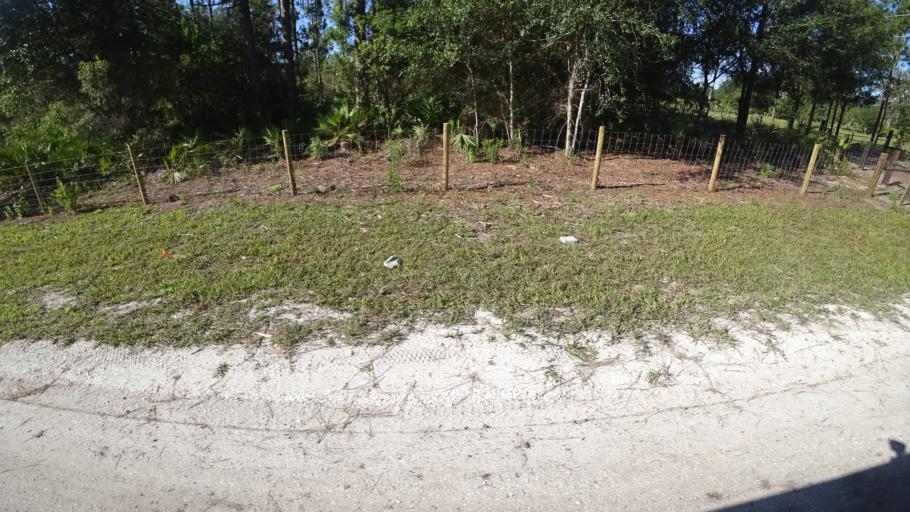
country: US
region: Florida
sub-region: Sarasota County
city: Fruitville
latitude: 27.4158
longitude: -82.2658
